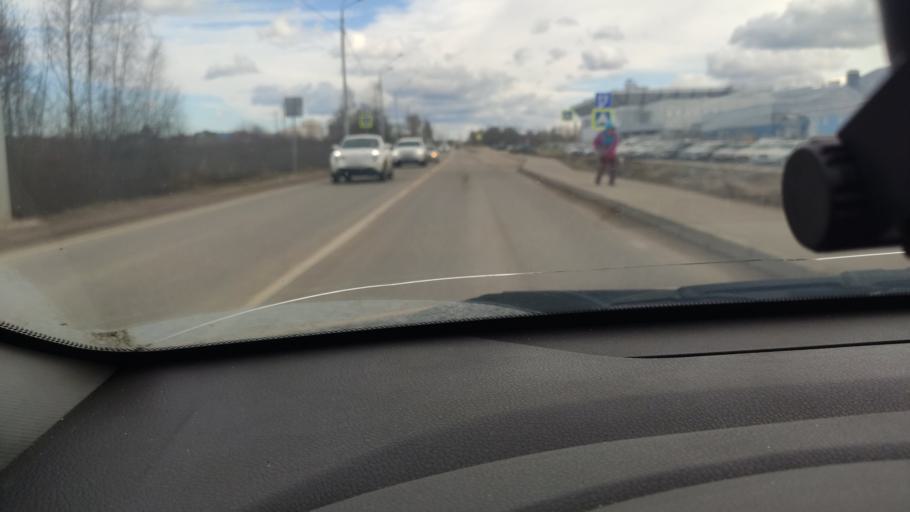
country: RU
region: Moskovskaya
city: Ruza
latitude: 55.7088
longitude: 36.1852
